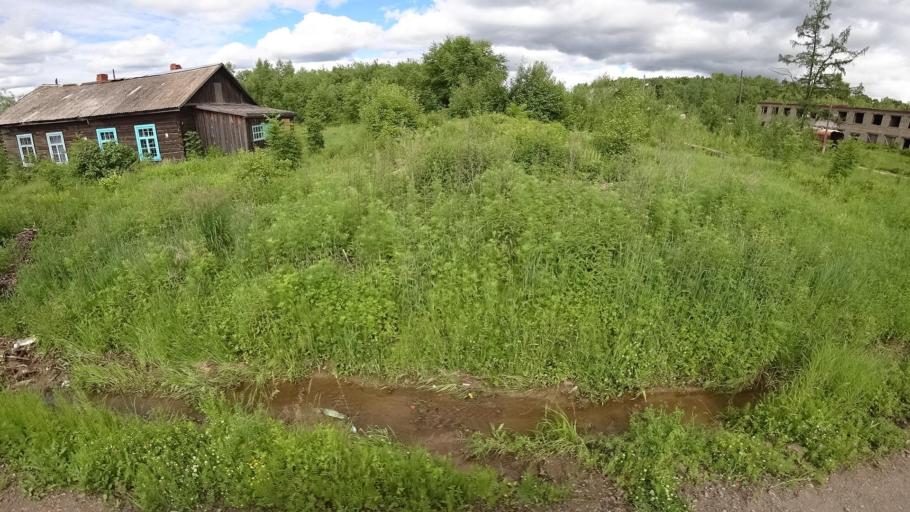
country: RU
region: Khabarovsk Krai
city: Litovko
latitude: 49.3685
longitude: 135.1734
